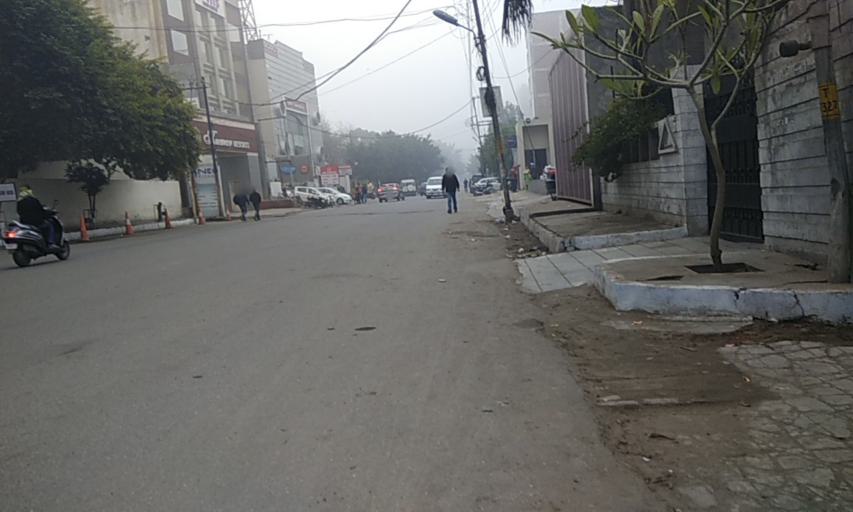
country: IN
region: Punjab
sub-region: Amritsar
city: Amritsar
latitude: 31.6413
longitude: 74.8668
